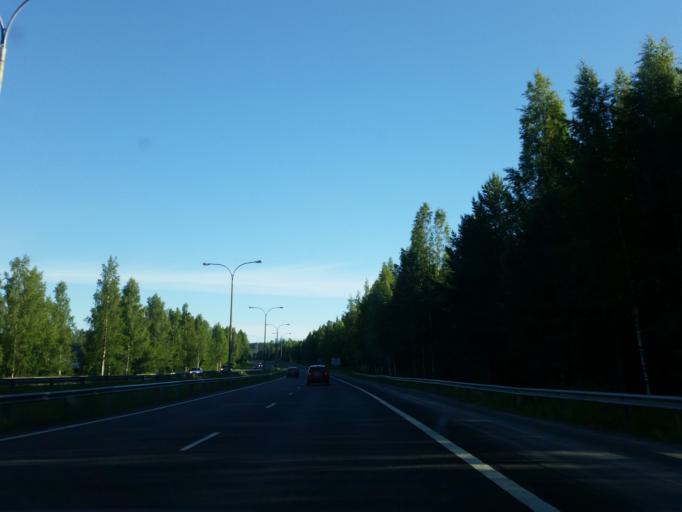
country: FI
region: Northern Savo
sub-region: Kuopio
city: Kuopio
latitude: 62.8739
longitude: 27.6212
